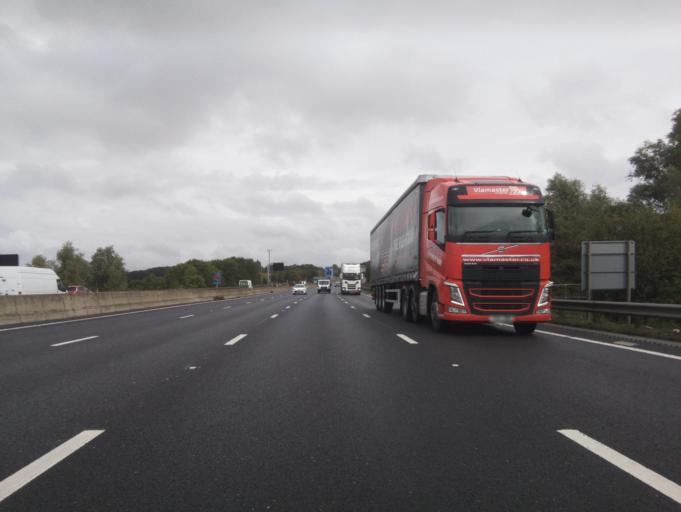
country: GB
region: England
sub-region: City and Borough of Wakefield
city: Ossett
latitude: 53.6967
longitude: -1.5573
